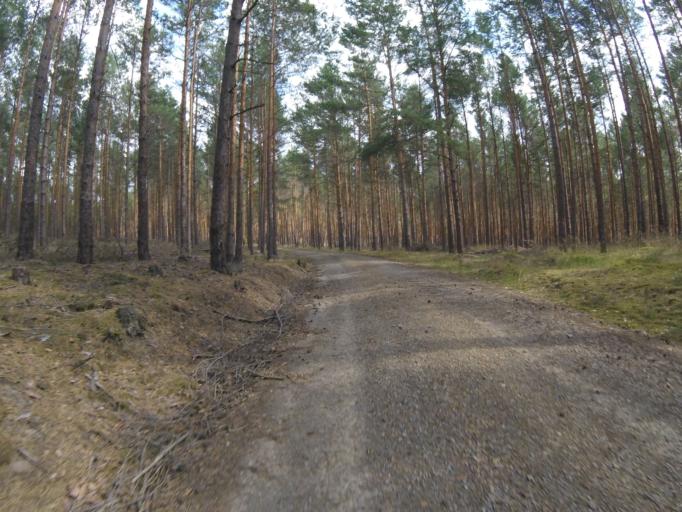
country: DE
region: Brandenburg
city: Halbe
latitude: 52.0580
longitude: 13.7665
